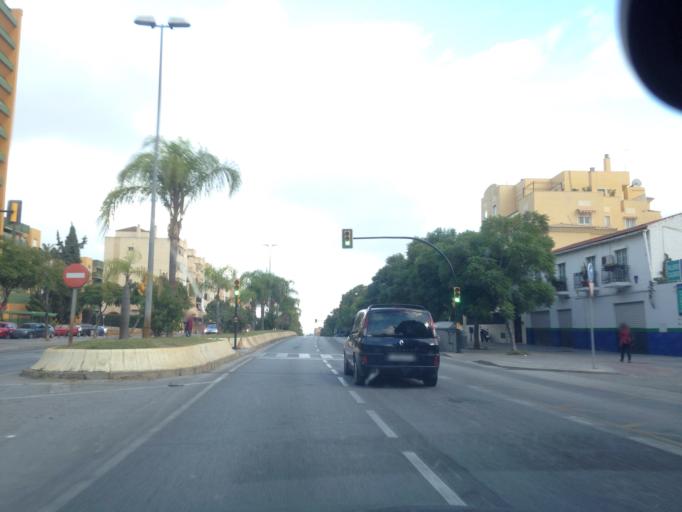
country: ES
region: Andalusia
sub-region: Provincia de Malaga
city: Malaga
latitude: 36.7254
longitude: -4.4587
